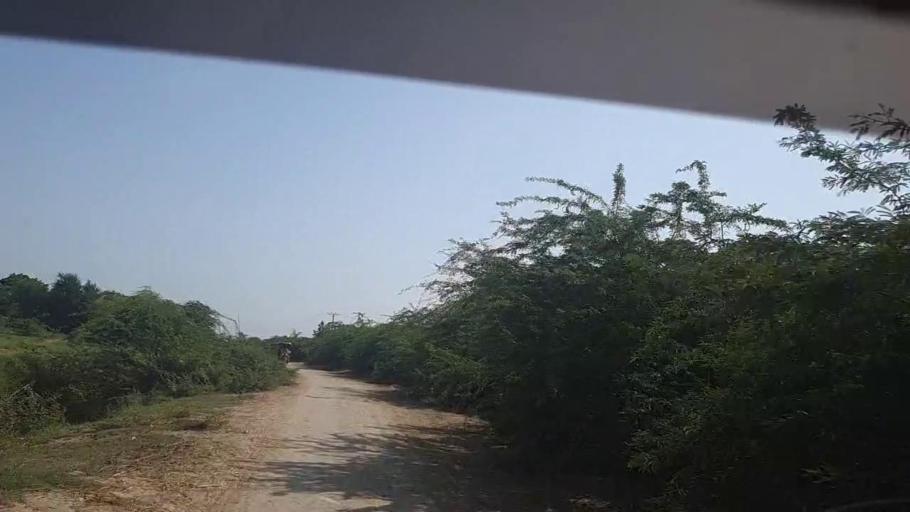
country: PK
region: Sindh
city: Rajo Khanani
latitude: 24.9627
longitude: 68.8915
